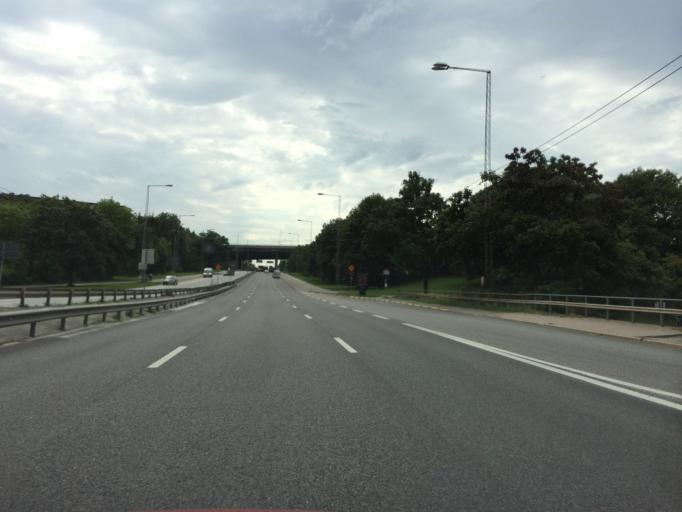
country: SE
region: Stockholm
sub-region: Stockholms Kommun
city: Arsta
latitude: 59.3068
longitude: 18.0223
